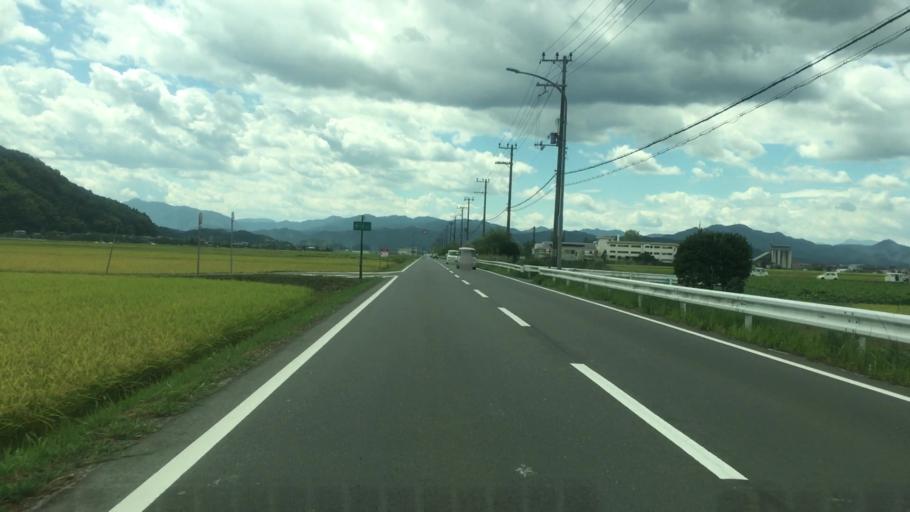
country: JP
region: Hyogo
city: Toyooka
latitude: 35.5354
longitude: 134.8397
